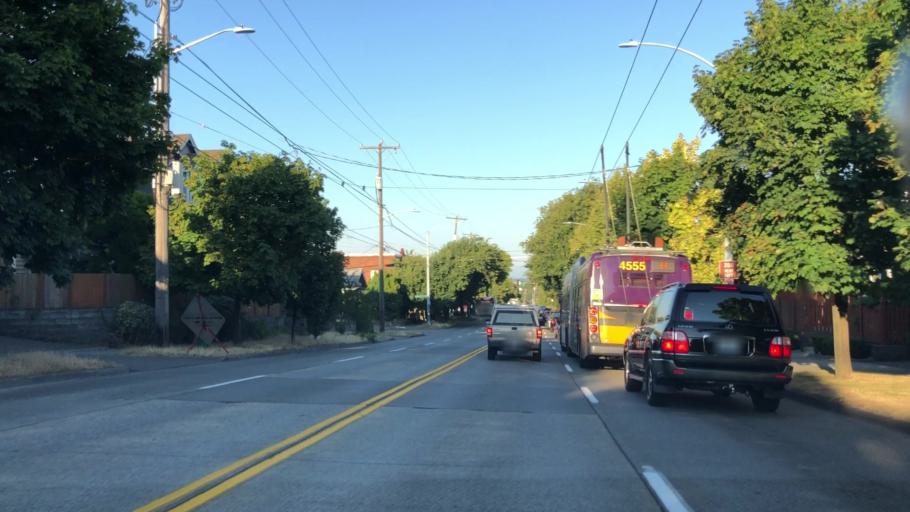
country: US
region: Washington
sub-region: King County
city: Seattle
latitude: 47.6621
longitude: -122.3525
